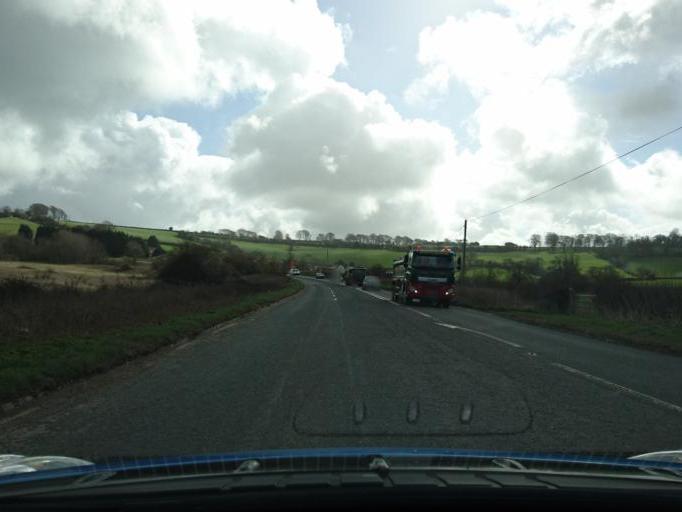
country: GB
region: England
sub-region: South Gloucestershire
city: Pucklechurch
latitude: 51.4501
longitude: -2.4065
